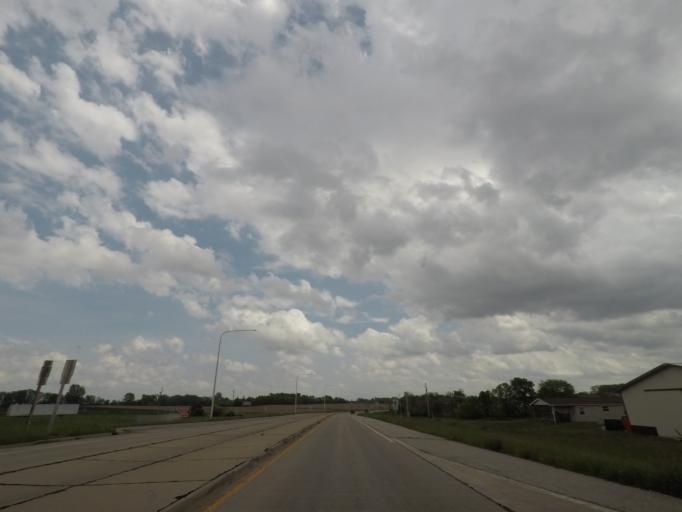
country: US
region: Illinois
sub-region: De Witt County
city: Clinton
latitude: 40.1746
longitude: -88.9623
